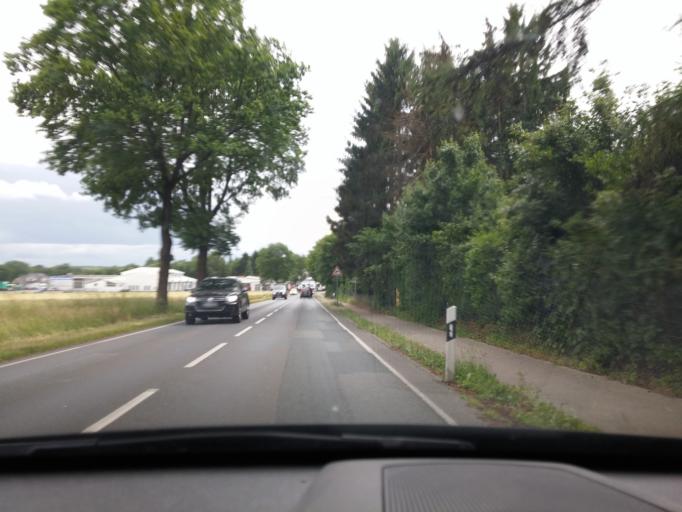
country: DE
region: Lower Saxony
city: Harmstorf
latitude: 53.3379
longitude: 9.9850
